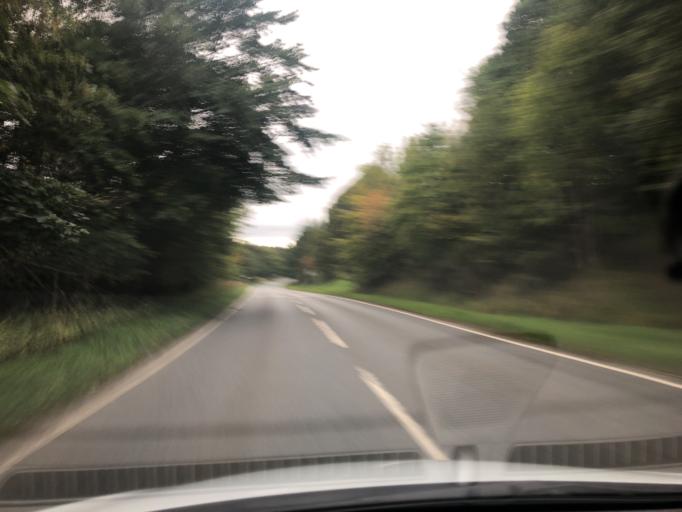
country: GB
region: Scotland
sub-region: Perth and Kinross
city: Pitlochry
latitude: 56.7512
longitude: -3.7991
